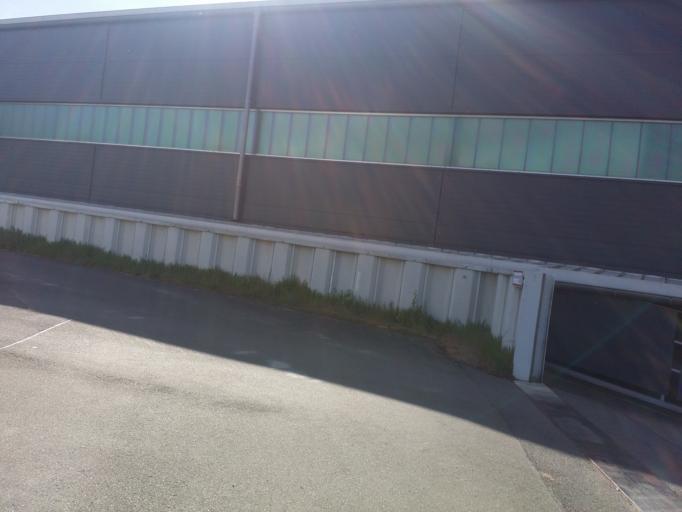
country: DE
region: Lower Saxony
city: Lemwerder
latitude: 53.1585
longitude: 8.6405
